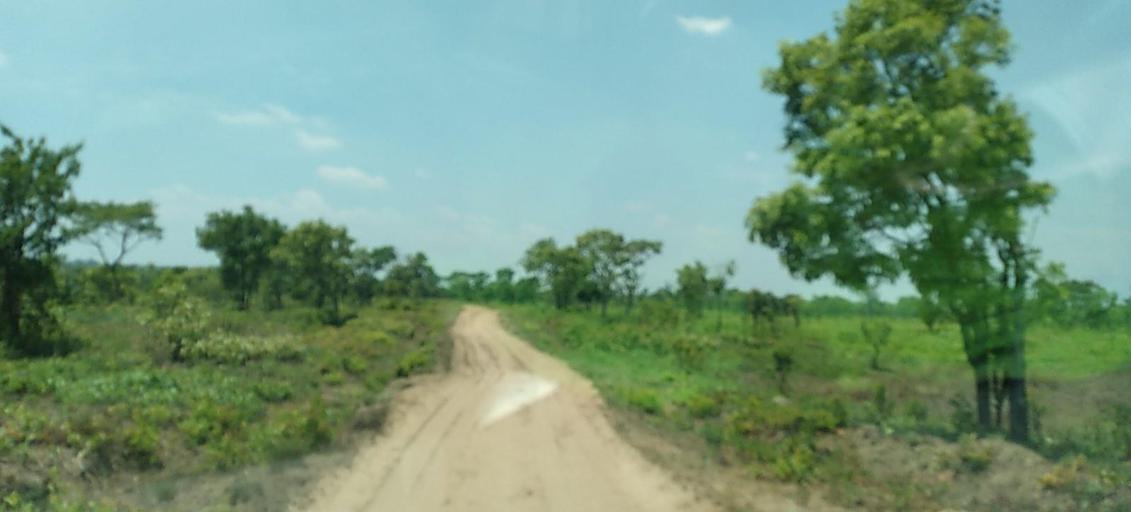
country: CD
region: Katanga
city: Kolwezi
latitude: -11.3351
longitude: 25.2252
